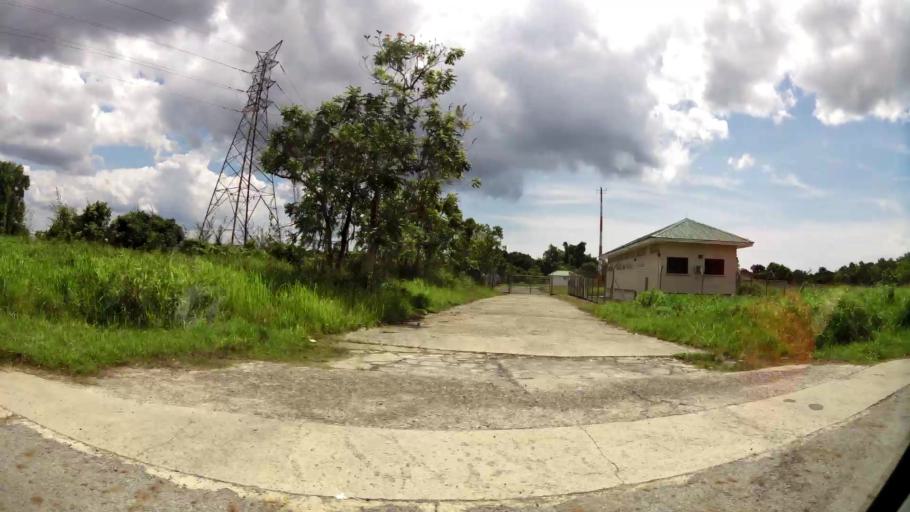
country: BN
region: Brunei and Muara
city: Bandar Seri Begawan
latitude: 4.9495
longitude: 114.9508
